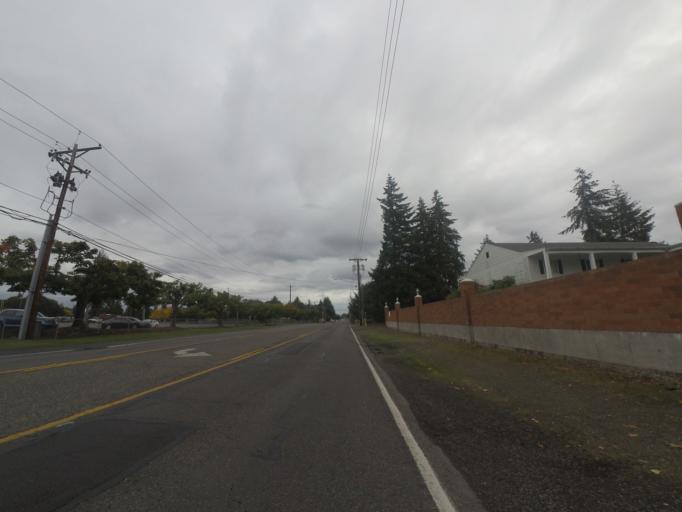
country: US
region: Washington
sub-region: Pierce County
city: Lakewood
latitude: 47.1557
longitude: -122.5185
